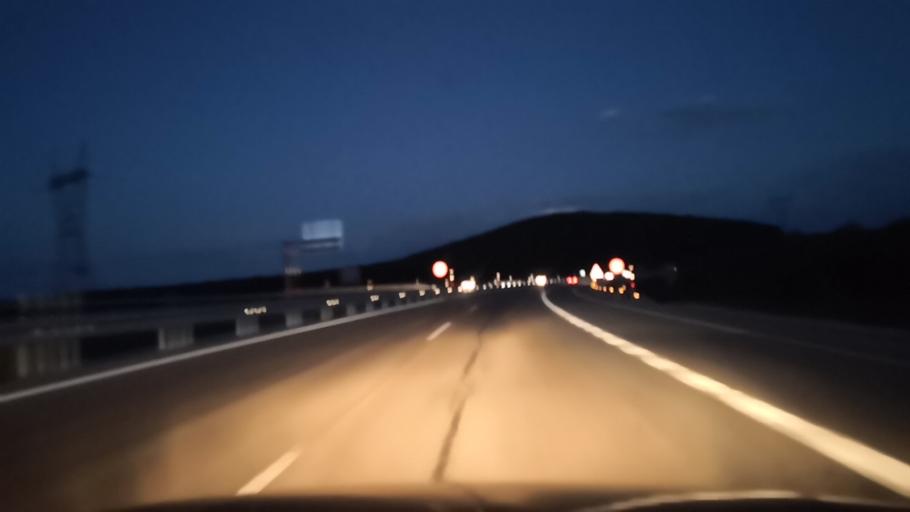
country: ES
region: Castille and Leon
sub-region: Provincia de Leon
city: Villagaton
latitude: 42.5997
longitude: -6.2286
